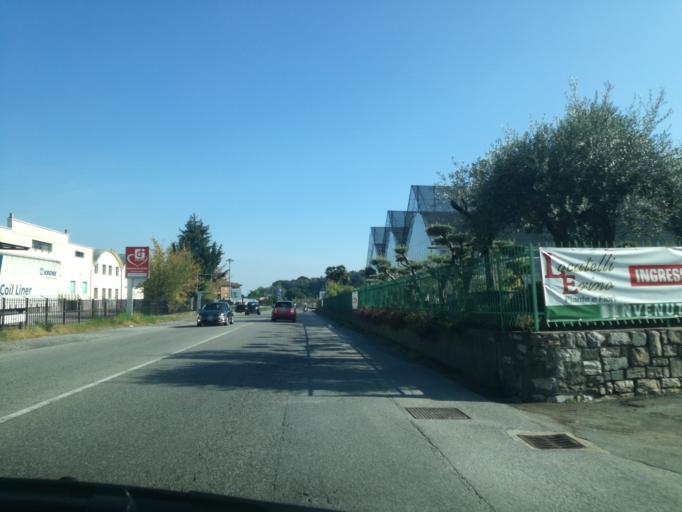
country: IT
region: Lombardy
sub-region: Provincia di Bergamo
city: Gromlongo
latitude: 45.7288
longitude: 9.5307
